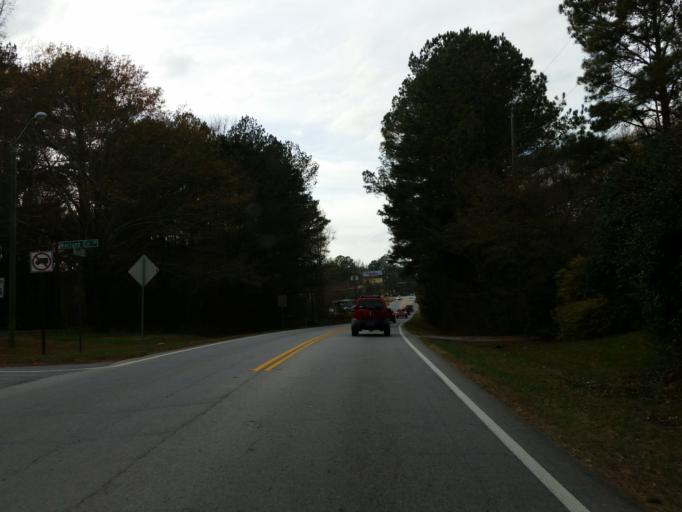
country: US
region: Georgia
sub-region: Paulding County
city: Hiram
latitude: 33.9033
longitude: -84.7223
